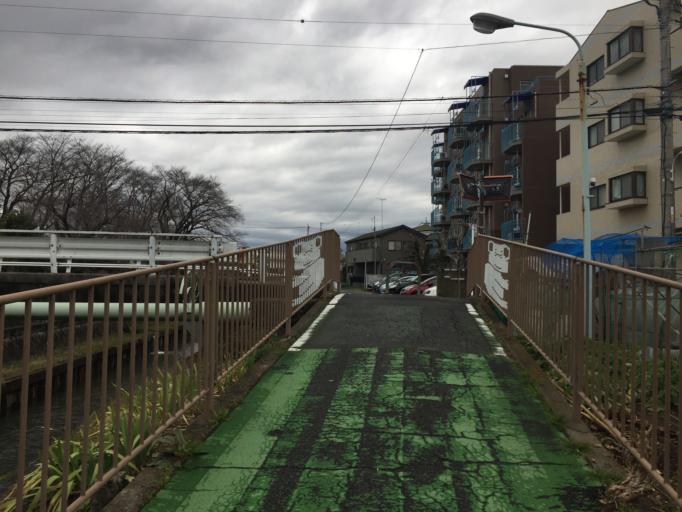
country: JP
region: Saitama
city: Yono
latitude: 35.8533
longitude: 139.6359
